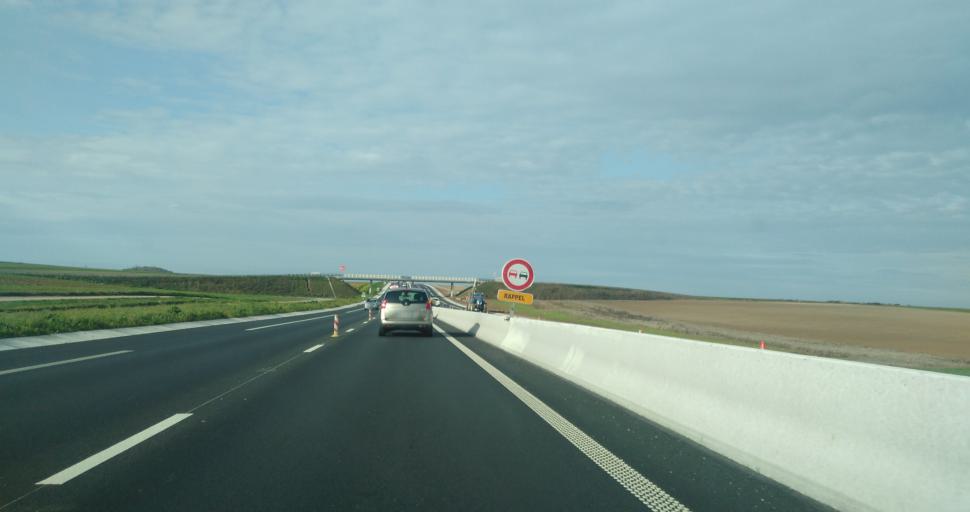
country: FR
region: Nord-Pas-de-Calais
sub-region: Departement du Pas-de-Calais
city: Aubigny-en-Artois
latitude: 50.3367
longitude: 2.6198
